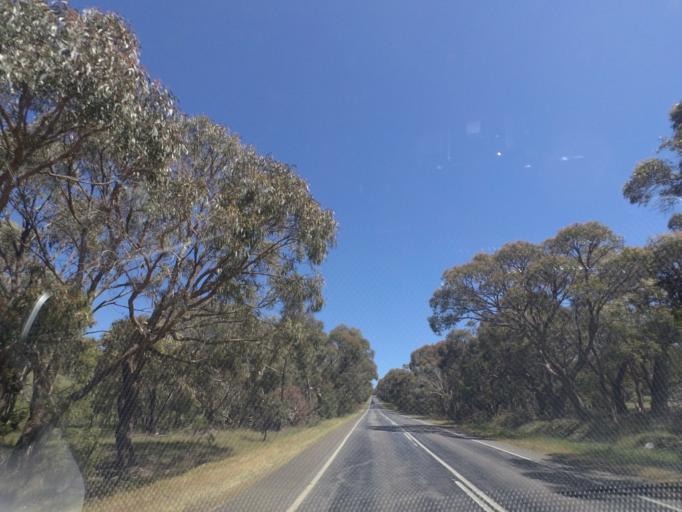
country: AU
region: Victoria
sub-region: Hume
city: Sunbury
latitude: -37.2985
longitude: 144.8132
